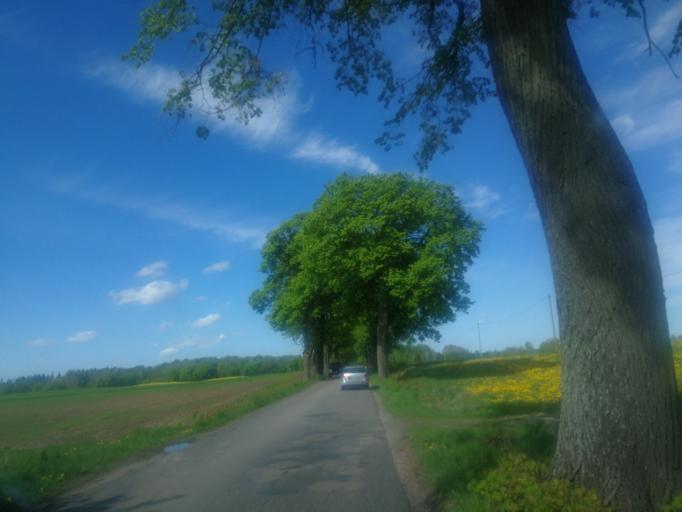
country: PL
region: Warmian-Masurian Voivodeship
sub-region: Powiat ilawski
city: Zalewo
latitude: 53.7421
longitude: 19.6983
